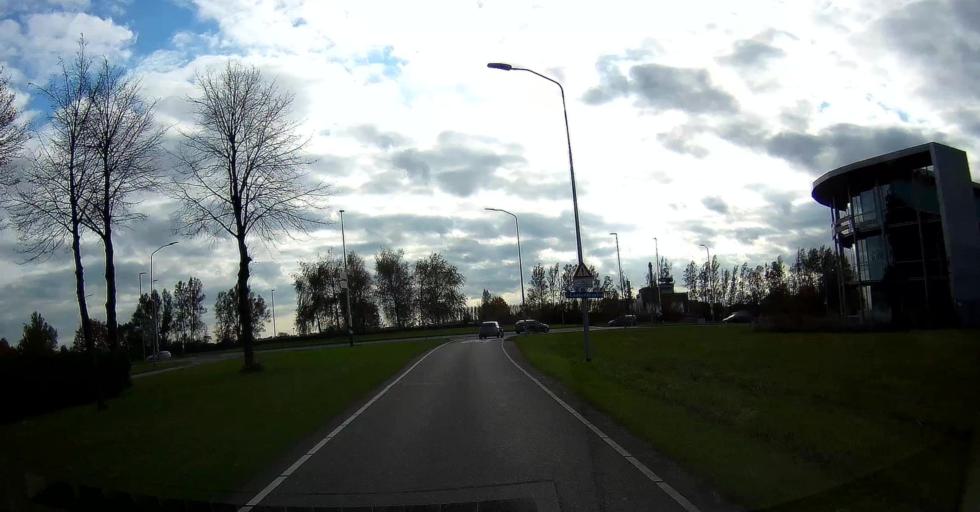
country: NL
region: Flevoland
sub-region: Gemeente Lelystad
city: Lelystad
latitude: 52.4948
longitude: 5.4749
